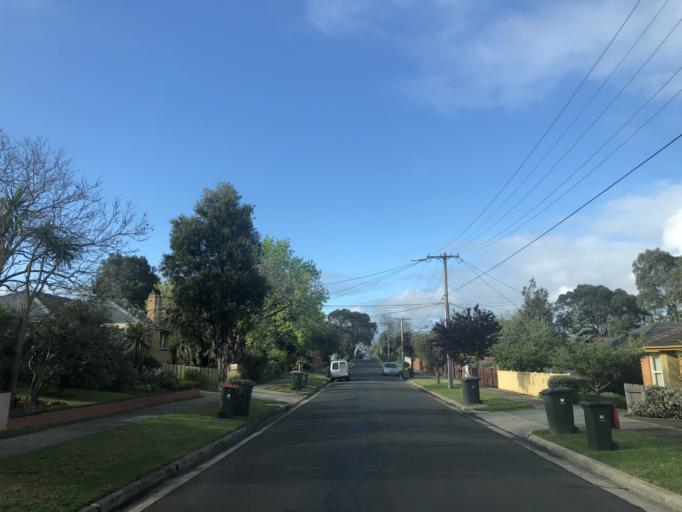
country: AU
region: Victoria
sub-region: Monash
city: Chadstone
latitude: -37.8860
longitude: 145.1183
